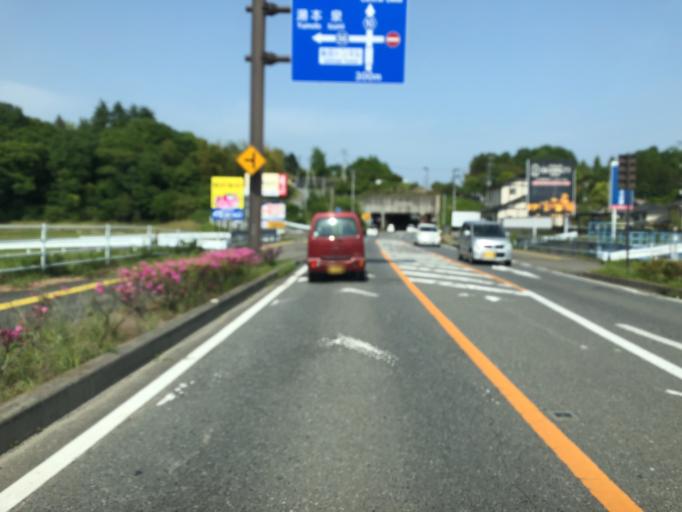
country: JP
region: Ibaraki
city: Kitaibaraki
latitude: 36.9235
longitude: 140.7884
